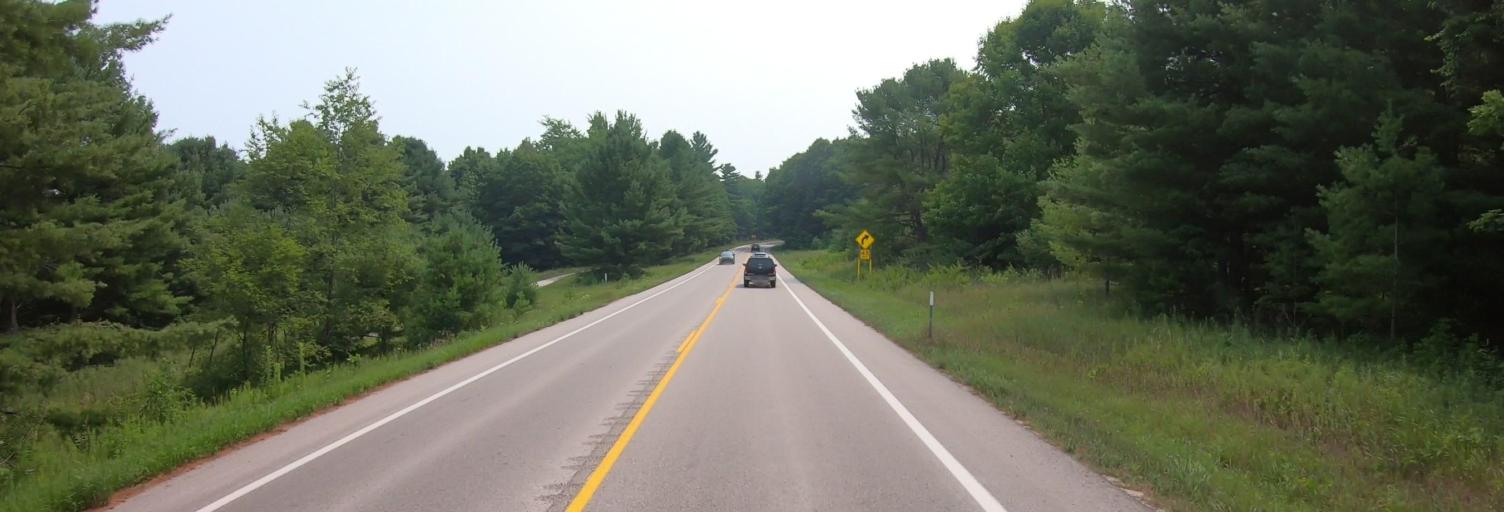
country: US
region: Michigan
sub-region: Leelanau County
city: Leland
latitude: 44.9334
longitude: -85.8952
